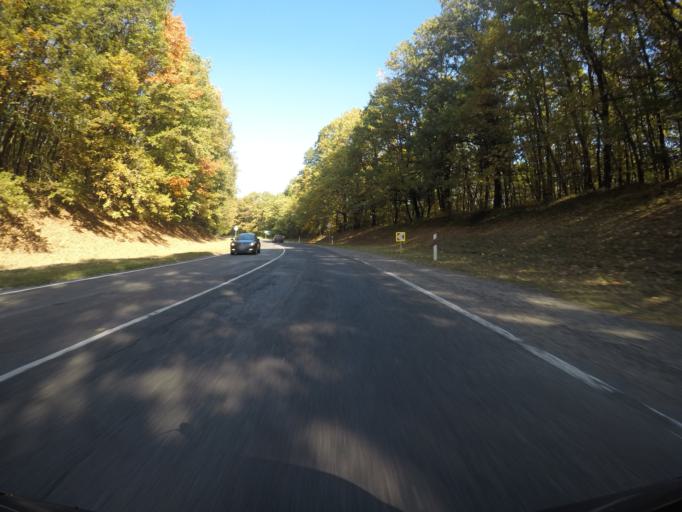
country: HU
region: Baranya
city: Mecseknadasd
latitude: 46.1916
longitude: 18.4528
